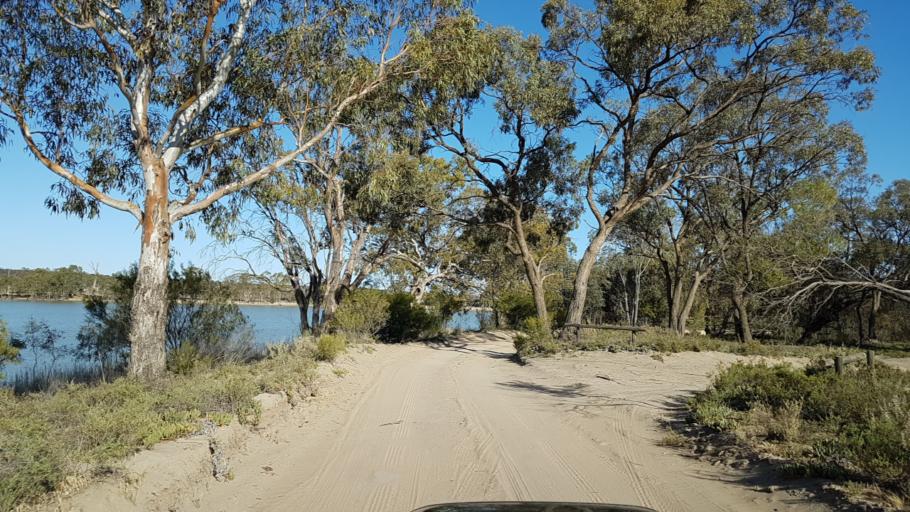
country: AU
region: South Australia
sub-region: Loxton Waikerie
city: Waikerie
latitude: -34.1604
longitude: 140.0305
